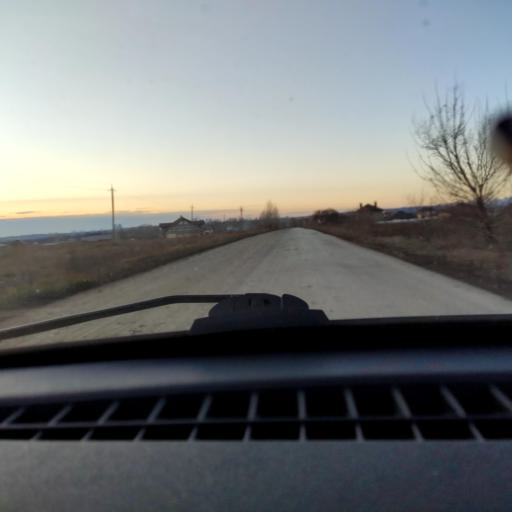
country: RU
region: Bashkortostan
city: Ufa
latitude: 54.7046
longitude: 56.1135
